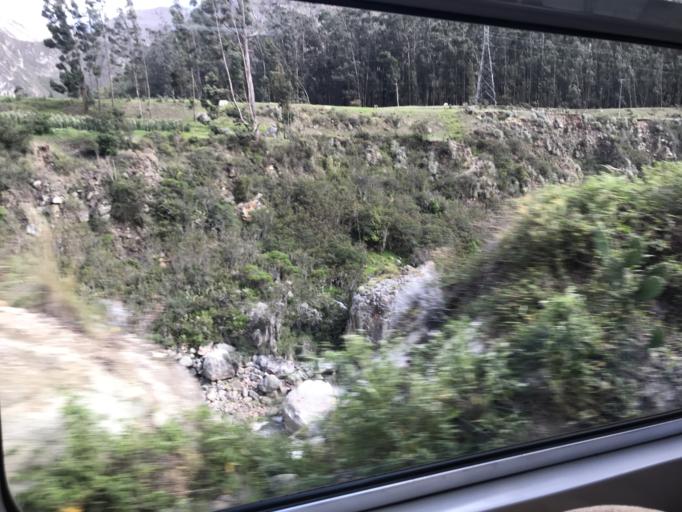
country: PE
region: Cusco
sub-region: Provincia de Urubamba
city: Ollantaytambo
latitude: -13.2252
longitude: -72.4286
